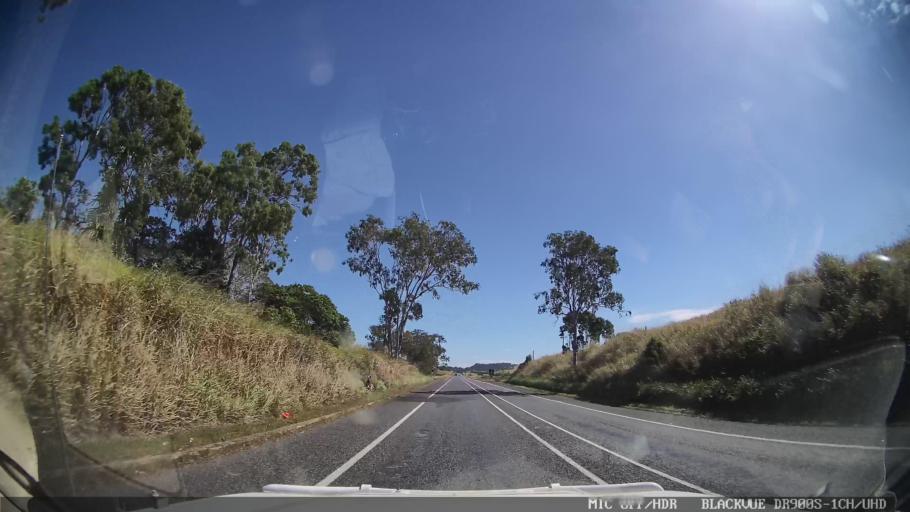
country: AU
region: Queensland
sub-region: Mackay
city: Walkerston
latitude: -21.0908
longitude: 149.0531
